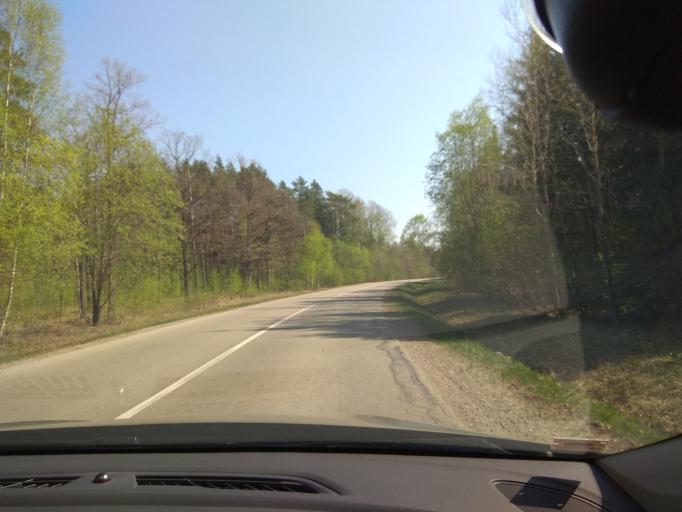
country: LT
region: Panevezys
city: Pasvalys
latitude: 55.9764
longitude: 24.1951
